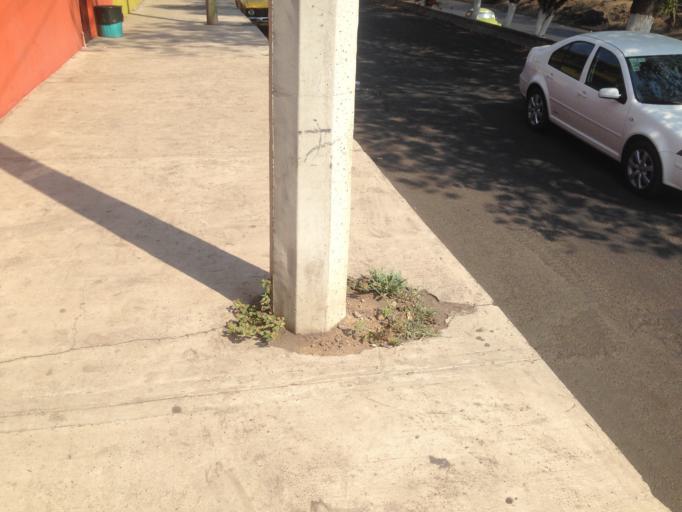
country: MX
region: Michoacan
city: Morelia
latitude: 19.7045
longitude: -101.2179
